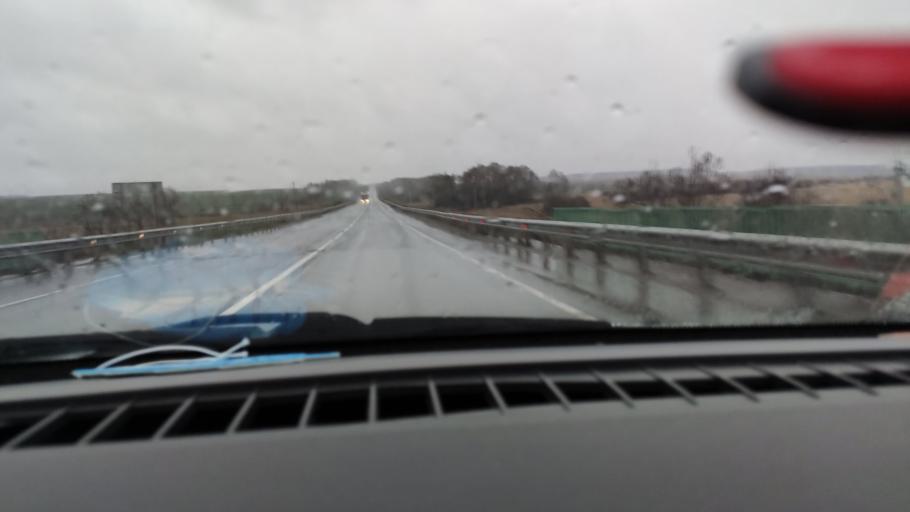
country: RU
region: Tatarstan
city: Mendeleyevsk
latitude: 55.9370
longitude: 52.2875
